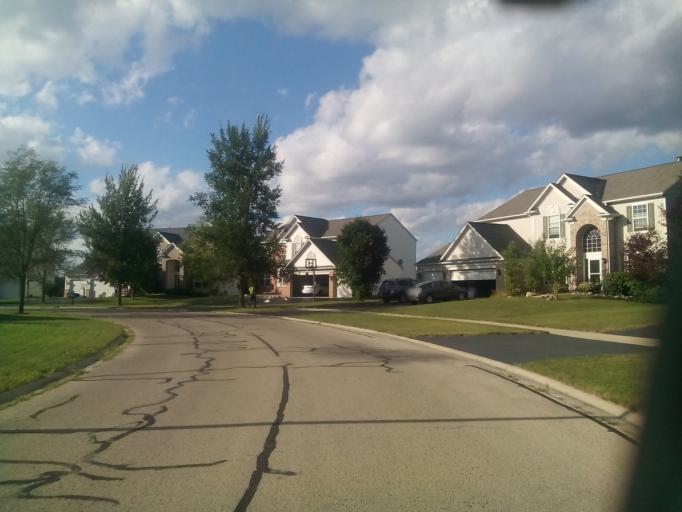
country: US
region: Illinois
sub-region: Will County
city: Bolingbrook
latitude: 41.7035
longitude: -88.1363
